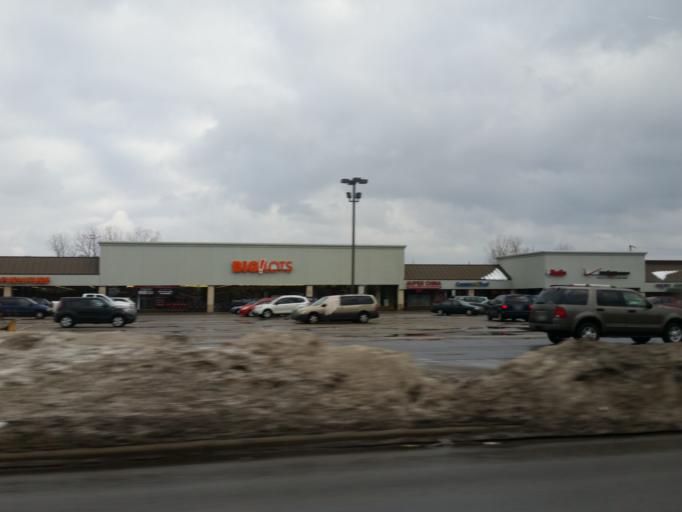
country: US
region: Ohio
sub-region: Summit County
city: Barberton
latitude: 41.0148
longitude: -81.6057
